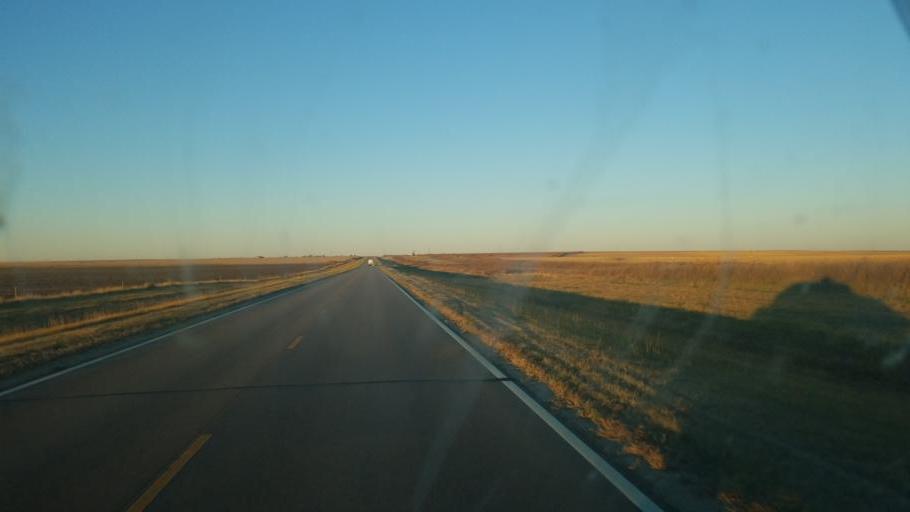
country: US
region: Kansas
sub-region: Wallace County
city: Sharon Springs
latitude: 38.8799
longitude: -101.9192
